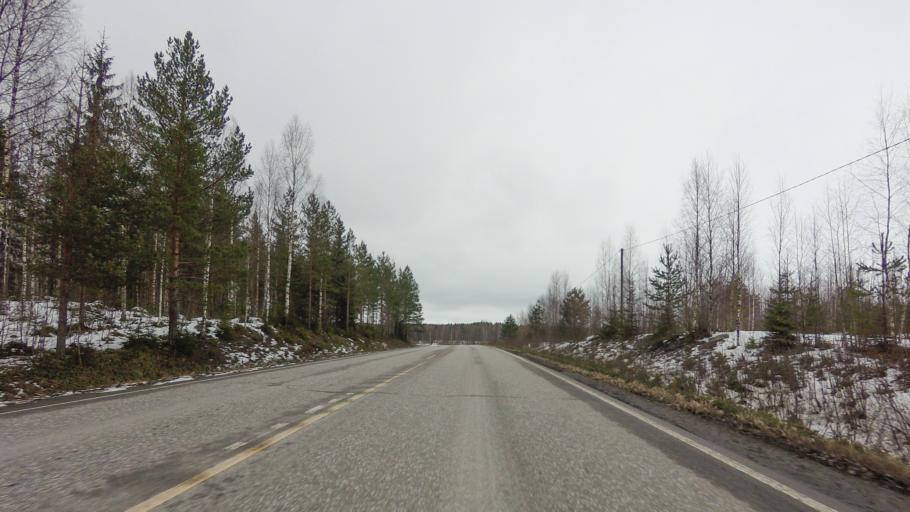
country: FI
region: Southern Savonia
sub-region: Savonlinna
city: Savonlinna
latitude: 61.8991
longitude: 28.9240
